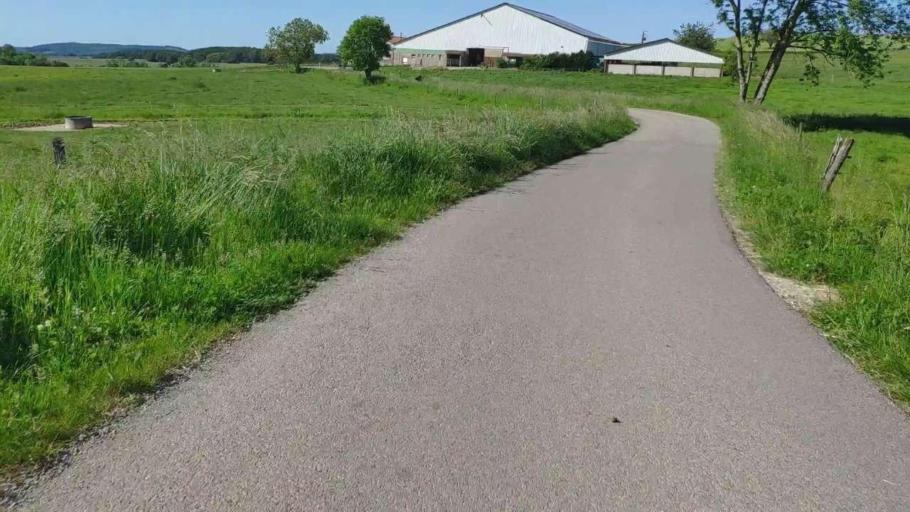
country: FR
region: Franche-Comte
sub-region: Departement du Jura
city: Perrigny
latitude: 46.7213
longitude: 5.5736
